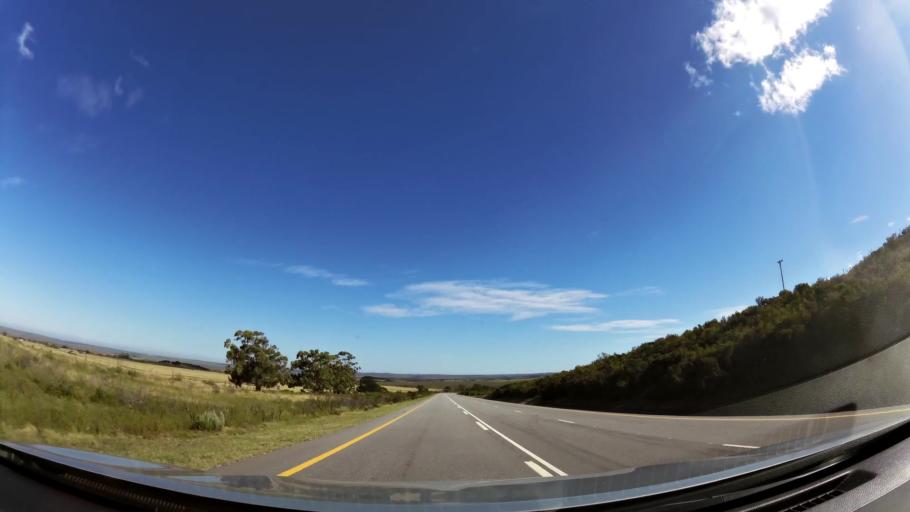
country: ZA
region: Eastern Cape
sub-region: Cacadu District Municipality
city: Kruisfontein
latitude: -34.0023
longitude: 24.6808
